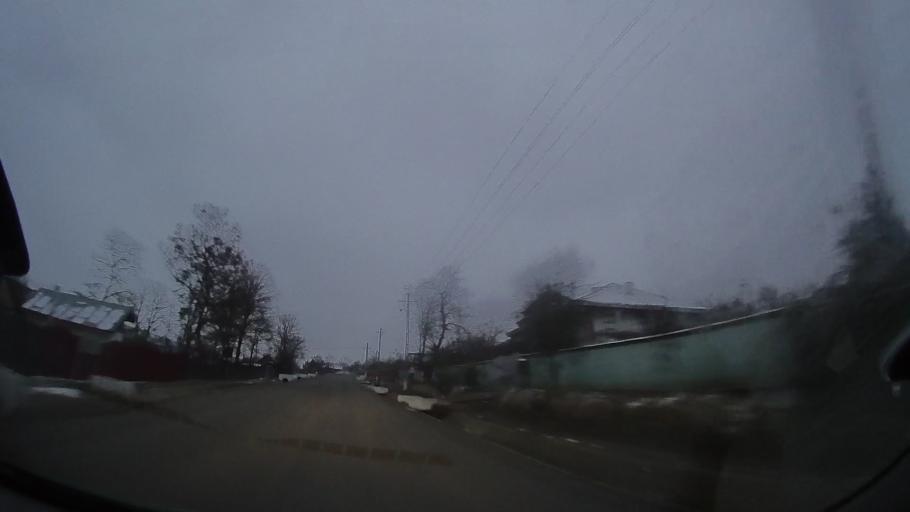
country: RO
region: Vaslui
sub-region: Comuna Gagesti
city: Gagesti
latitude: 46.3918
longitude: 27.9801
